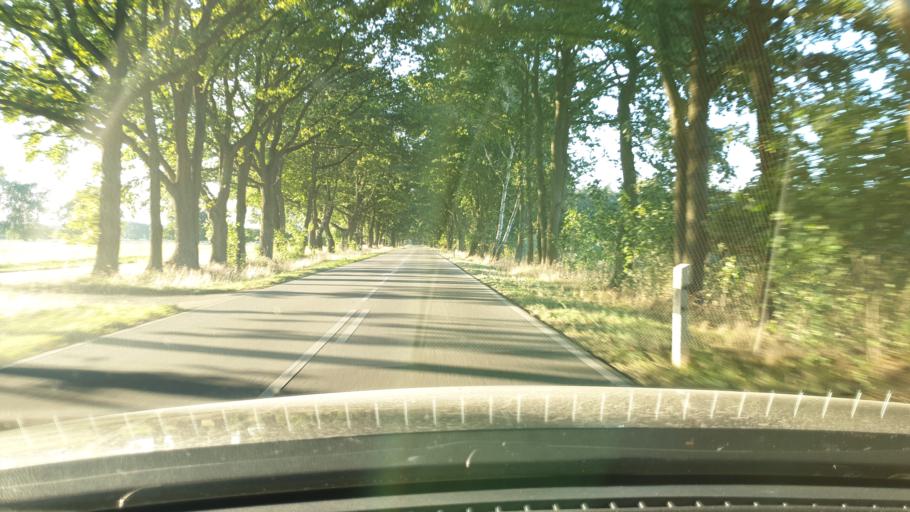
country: DE
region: Mecklenburg-Vorpommern
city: Wittenburg
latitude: 53.4923
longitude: 11.0149
